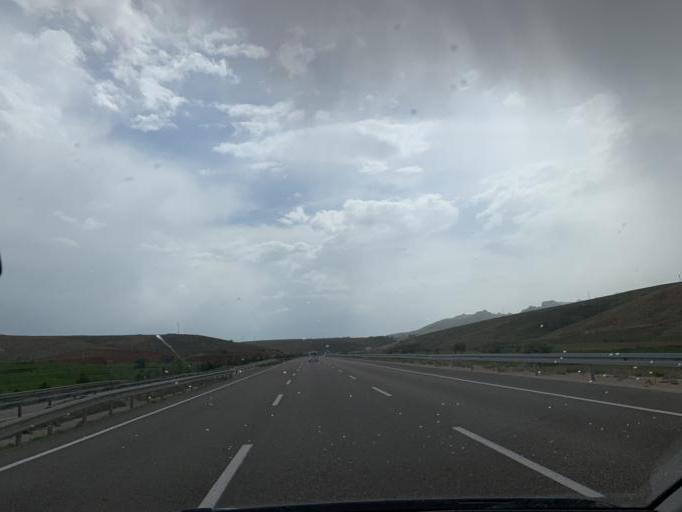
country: TR
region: Eskisehir
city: Sivrihisar
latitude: 39.4743
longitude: 31.5907
